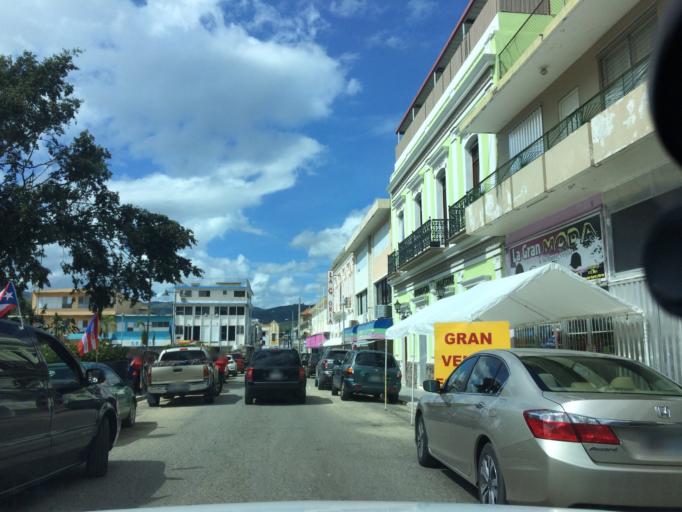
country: PR
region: Utuado
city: Utuado
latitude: 18.2656
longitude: -66.6996
